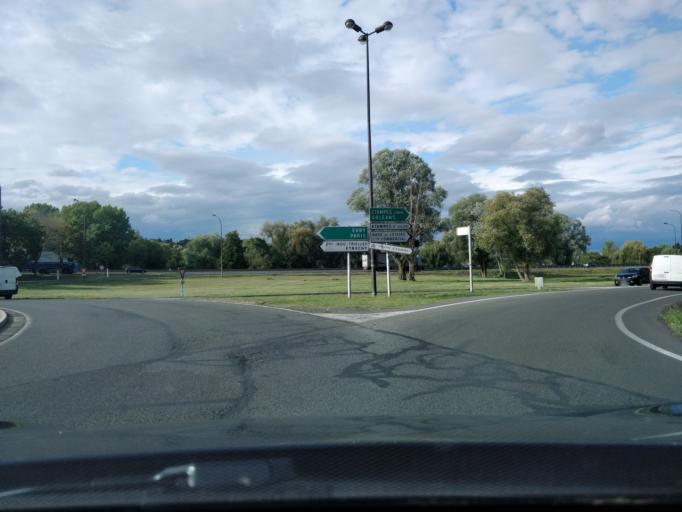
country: FR
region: Ile-de-France
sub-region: Departement de l'Essonne
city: Etampes
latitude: 48.4265
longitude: 2.1541
